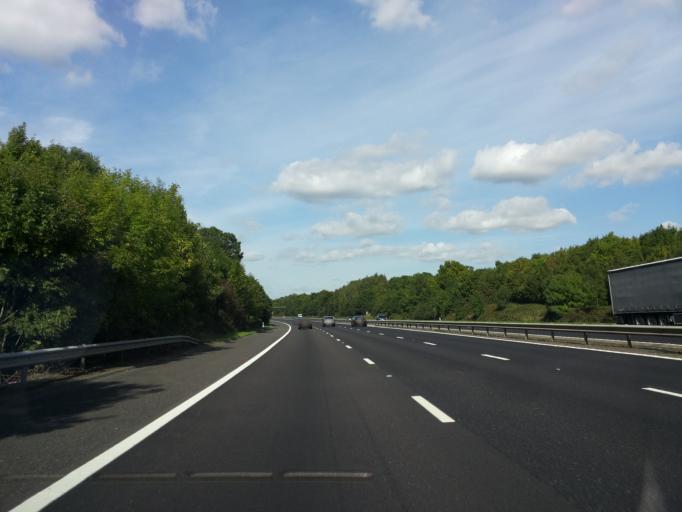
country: GB
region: England
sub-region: Kent
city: Longfield
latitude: 51.3445
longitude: 0.2759
